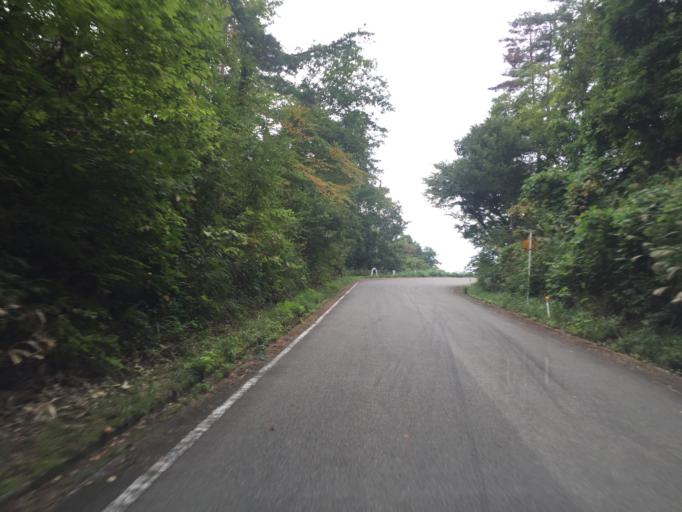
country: JP
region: Fukushima
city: Inawashiro
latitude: 37.4891
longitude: 139.9621
